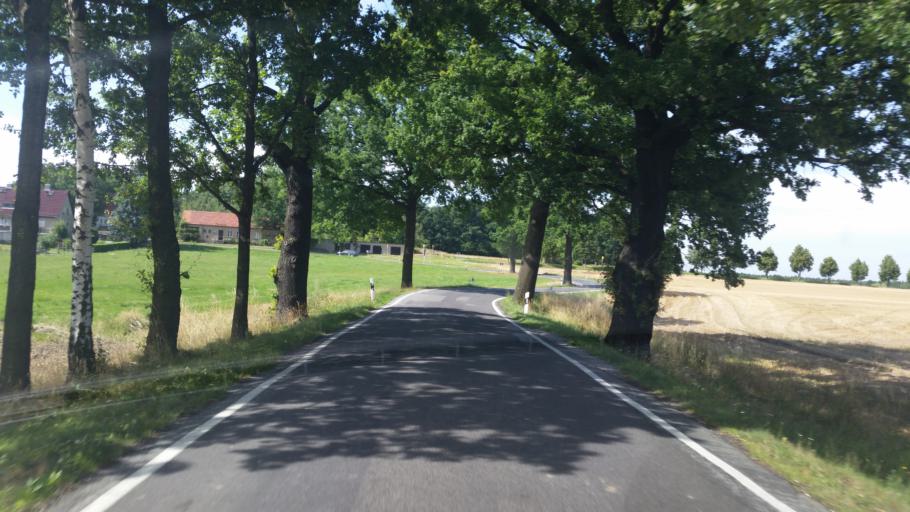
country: DE
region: Saxony
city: Schwepnitz
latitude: 51.3267
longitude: 14.0192
